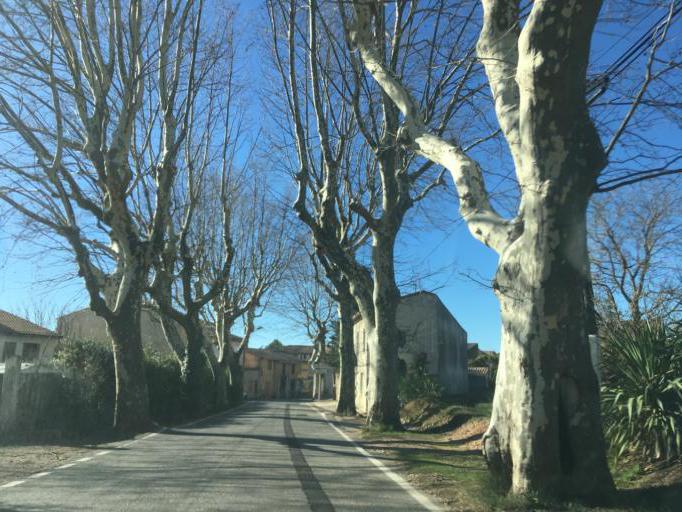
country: FR
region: Provence-Alpes-Cote d'Azur
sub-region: Departement du Var
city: Barjols
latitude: 43.5934
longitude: 6.0198
